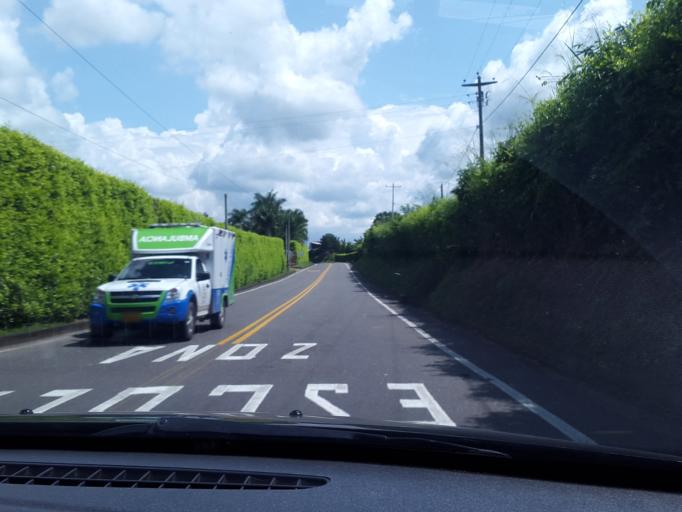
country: CO
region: Valle del Cauca
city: Alcala
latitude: 4.6878
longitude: -75.8184
